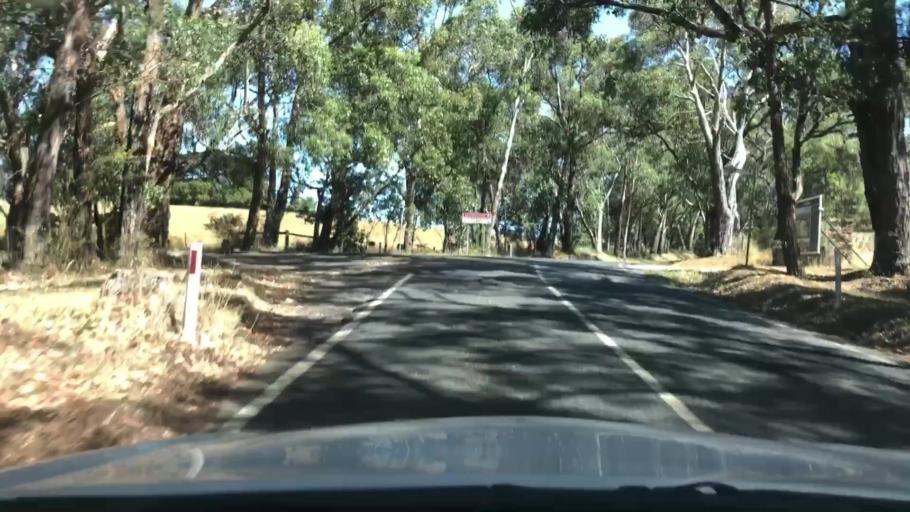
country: AU
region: Victoria
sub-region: Yarra Ranges
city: Macclesfield
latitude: -37.8635
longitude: 145.4790
